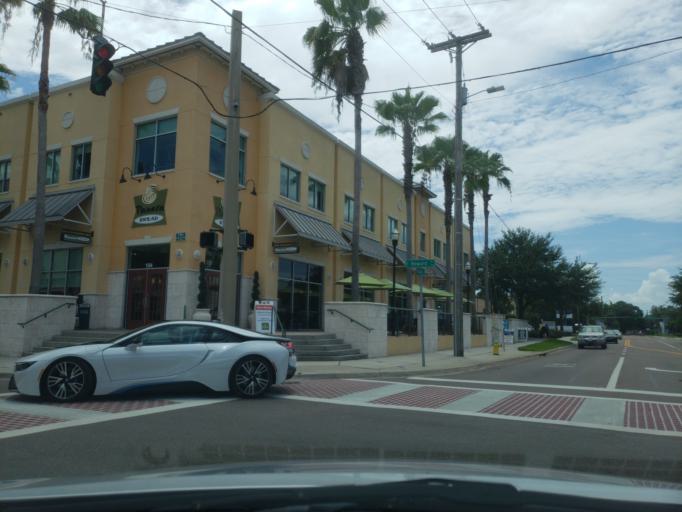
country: US
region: Florida
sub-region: Hillsborough County
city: Tampa
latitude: 27.9374
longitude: -82.4830
